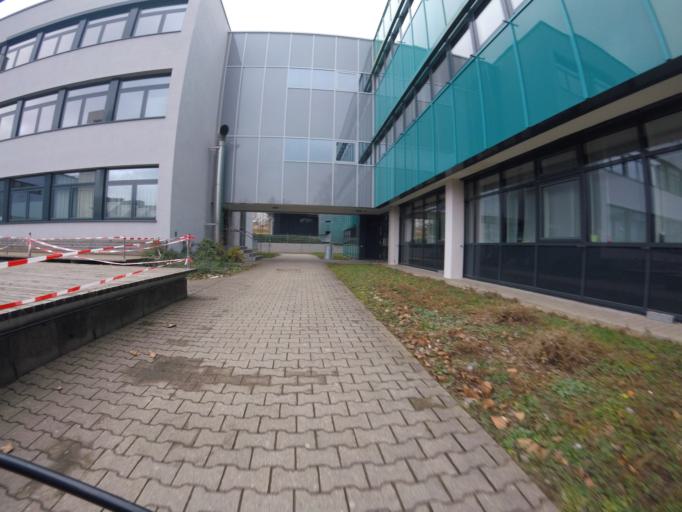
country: DE
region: Baden-Wuerttemberg
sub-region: Regierungsbezirk Stuttgart
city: Backnang
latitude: 48.9379
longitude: 9.4348
